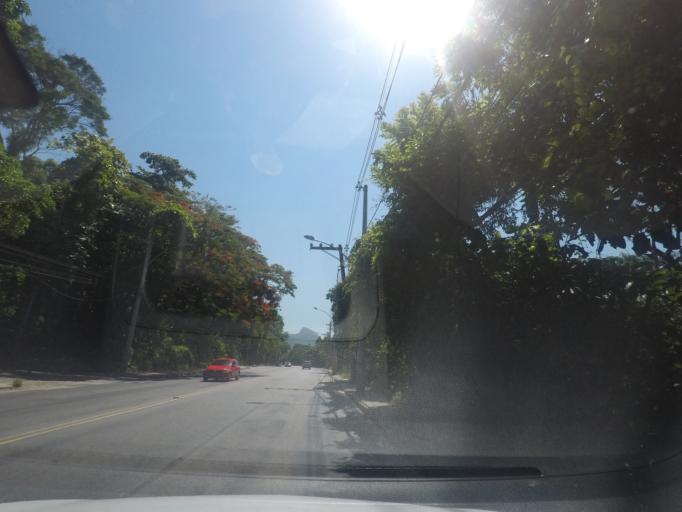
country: BR
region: Rio de Janeiro
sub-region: Nilopolis
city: Nilopolis
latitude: -22.9873
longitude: -43.4785
